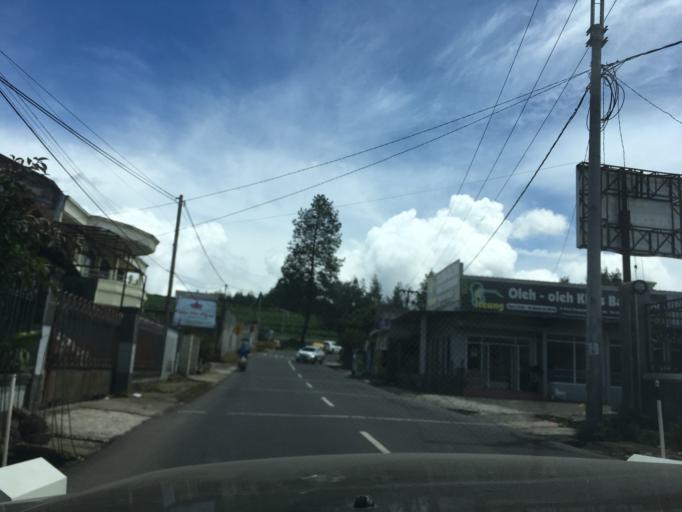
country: ID
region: West Java
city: Lembang
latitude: -6.8083
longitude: 107.6471
